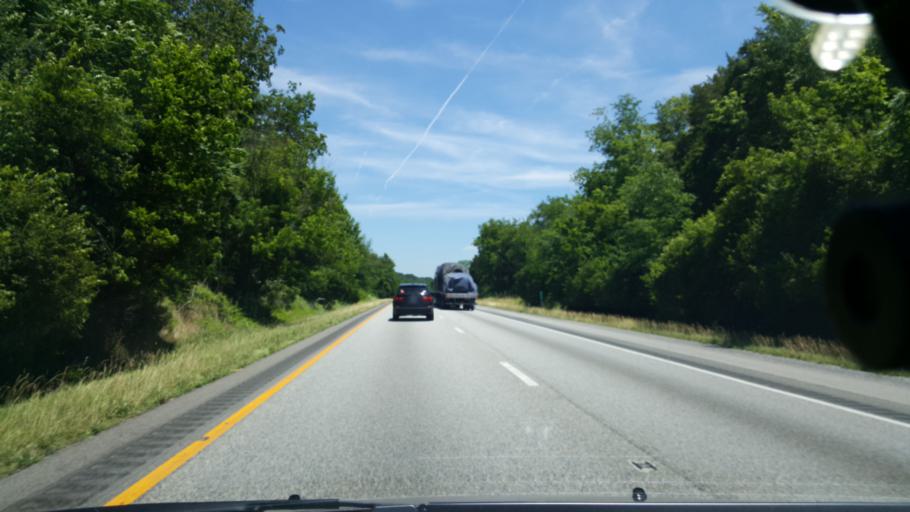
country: US
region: Virginia
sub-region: Botetourt County
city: Fincastle
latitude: 37.4546
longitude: -79.8436
